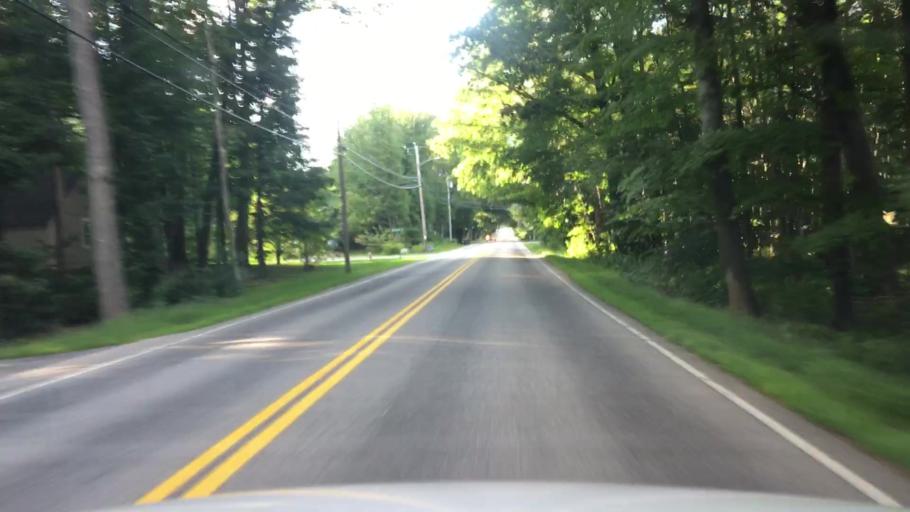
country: US
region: Maine
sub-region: Cumberland County
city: Scarborough
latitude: 43.5836
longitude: -70.2919
